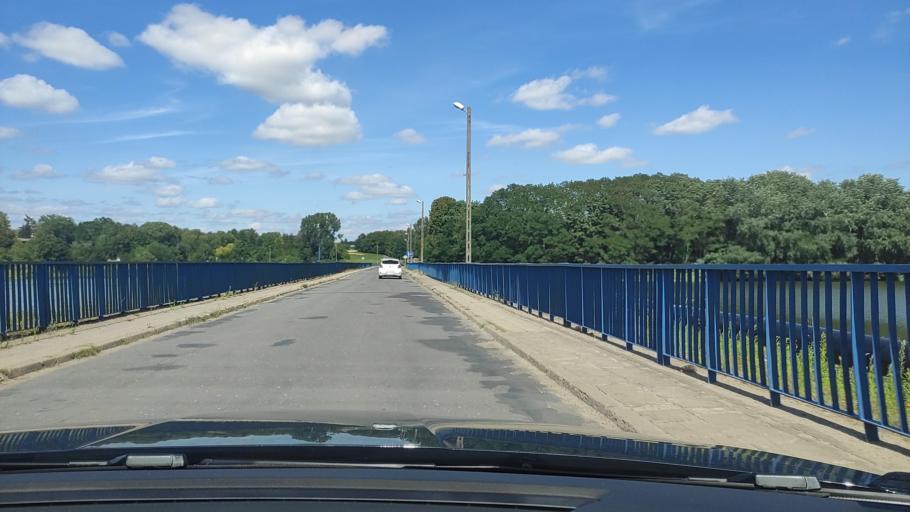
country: PL
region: Greater Poland Voivodeship
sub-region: Powiat poznanski
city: Kostrzyn
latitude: 52.4744
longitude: 17.1834
